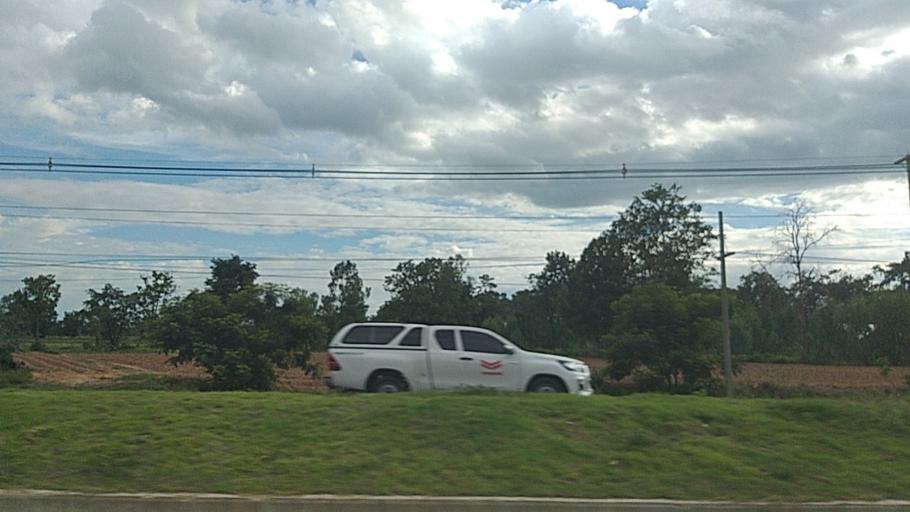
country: TH
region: Surin
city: Prasat
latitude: 14.5711
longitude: 103.4875
